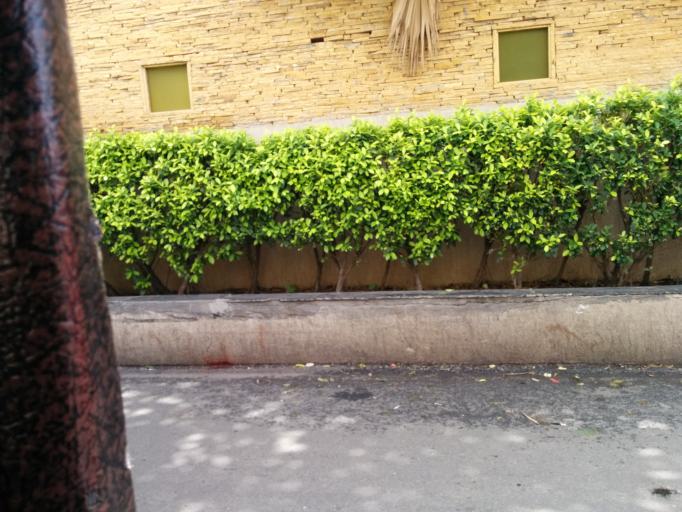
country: IN
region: Maharashtra
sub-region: Pune Division
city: Lohogaon
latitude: 18.5601
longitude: 73.9117
